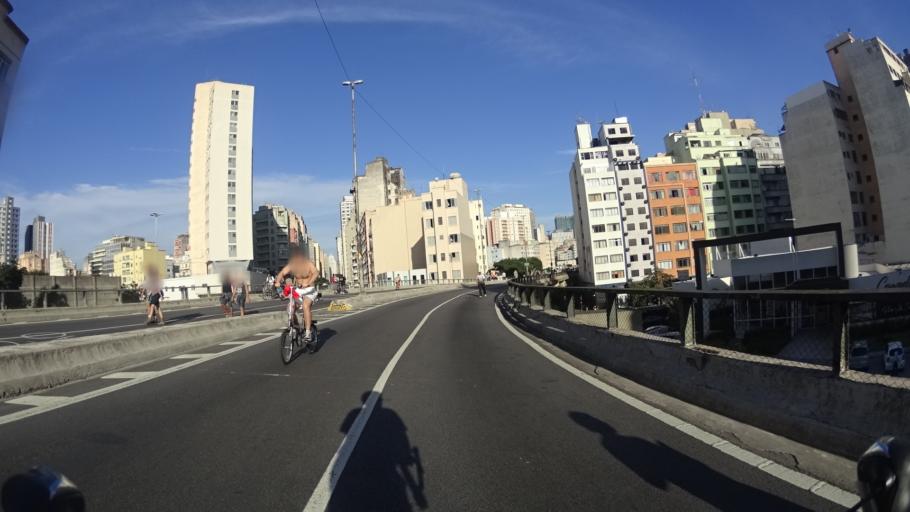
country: BR
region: Sao Paulo
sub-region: Sao Paulo
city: Sao Paulo
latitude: -23.5366
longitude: -46.6492
